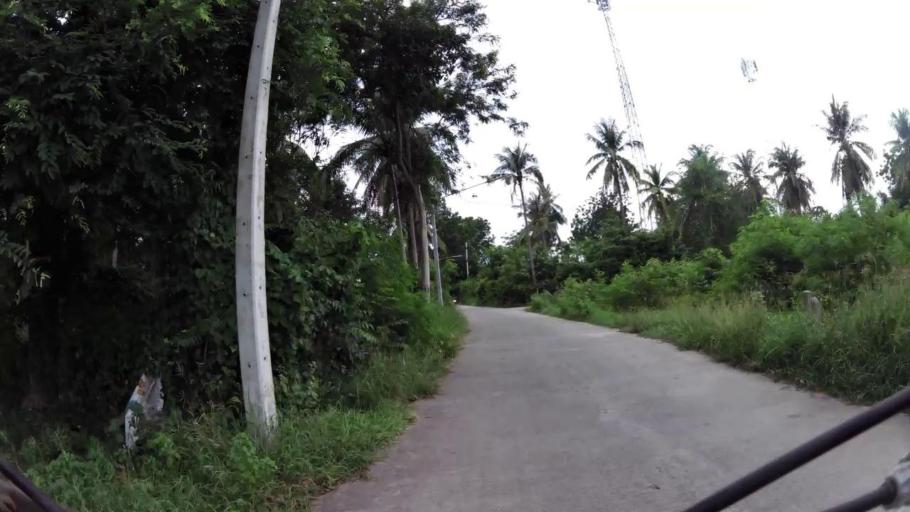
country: TH
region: Prachuap Khiri Khan
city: Prachuap Khiri Khan
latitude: 11.7403
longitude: 99.7775
